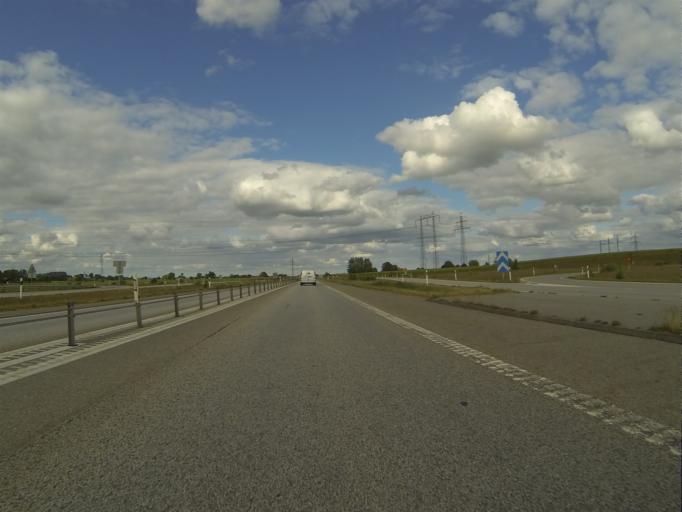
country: SE
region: Skane
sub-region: Burlovs Kommun
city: Arloev
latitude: 55.6158
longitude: 13.1227
